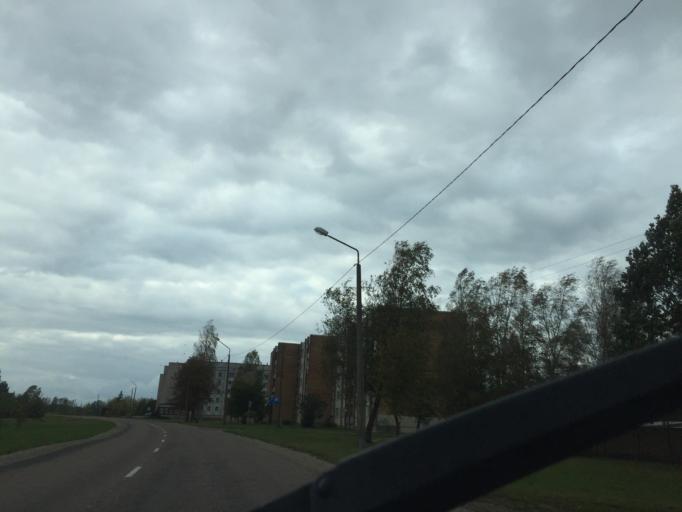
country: LV
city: Tireli
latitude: 56.7990
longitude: 23.6113
